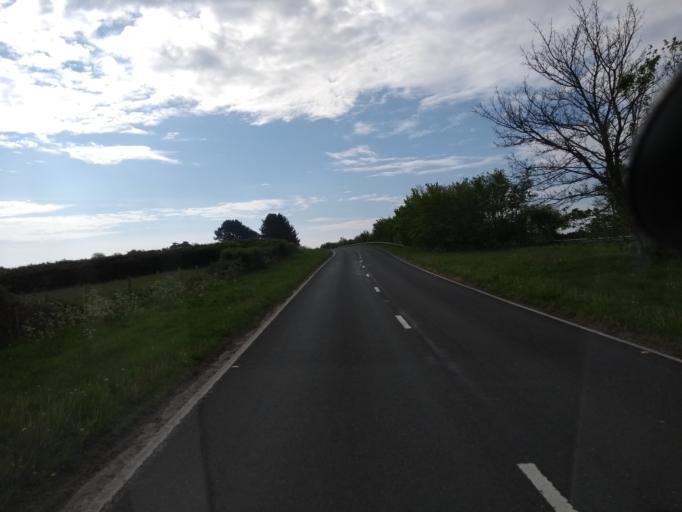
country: GB
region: England
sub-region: Dorset
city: Lyme Regis
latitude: 50.7563
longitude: -2.9379
